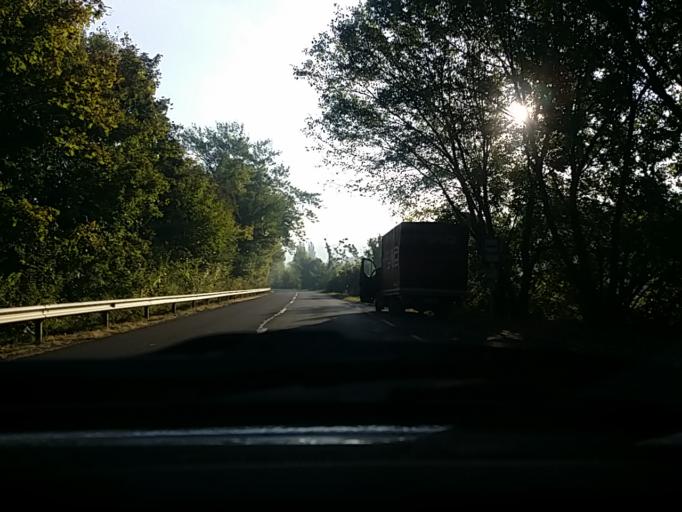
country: HU
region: Pest
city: Nagymaros
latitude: 47.7610
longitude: 18.9321
